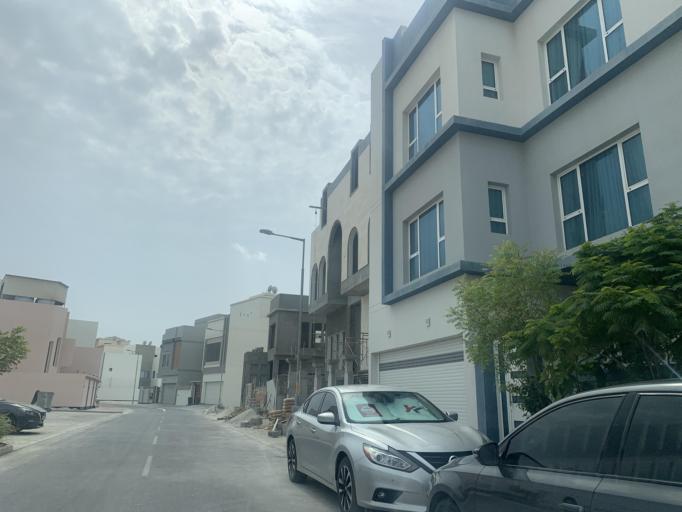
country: BH
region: Muharraq
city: Al Muharraq
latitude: 26.2868
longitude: 50.6369
